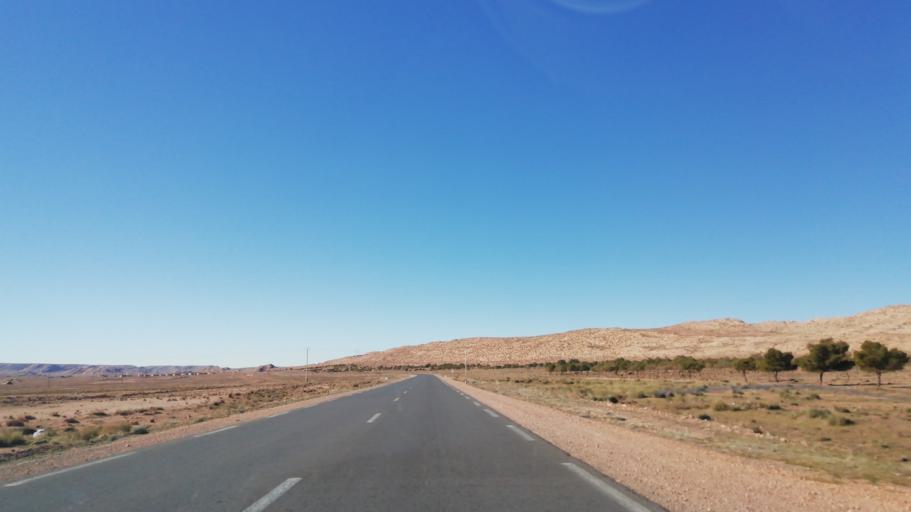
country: DZ
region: El Bayadh
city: El Bayadh
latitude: 33.6175
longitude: 1.1914
